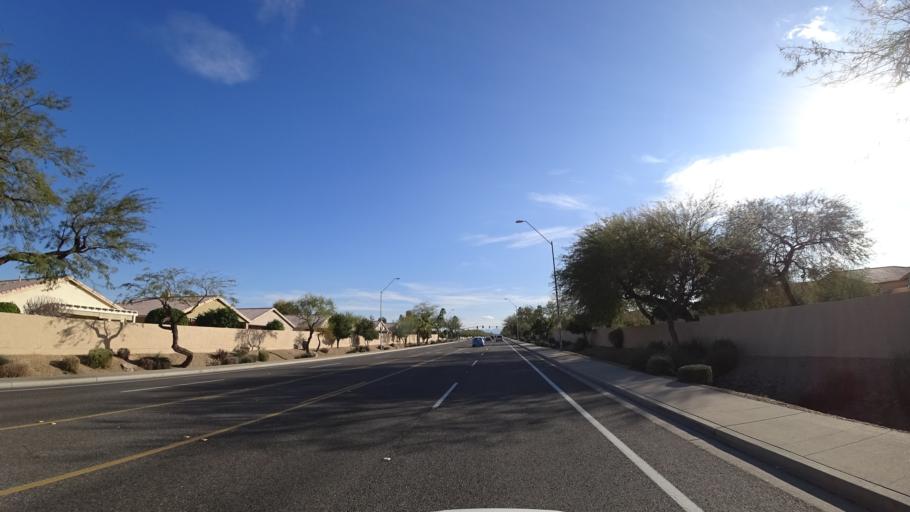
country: US
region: Arizona
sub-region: Maricopa County
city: Sun City
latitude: 33.6655
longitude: -112.2551
